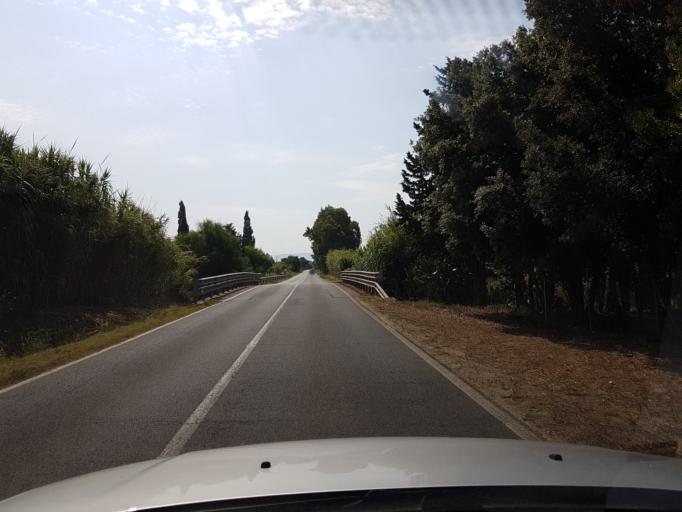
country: IT
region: Sardinia
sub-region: Provincia di Oristano
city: Donigala Fenugheddu
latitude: 39.9473
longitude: 8.5646
